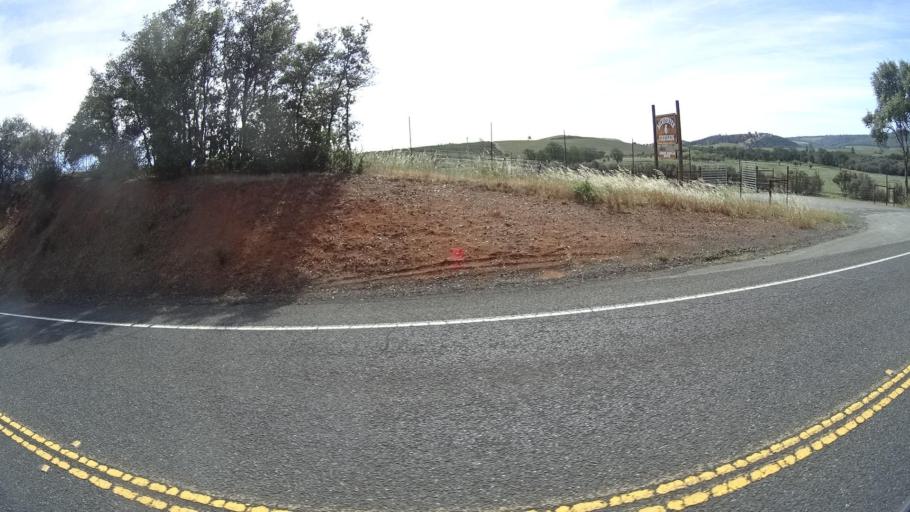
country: US
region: California
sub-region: Lake County
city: Soda Bay
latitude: 38.9349
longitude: -122.7404
